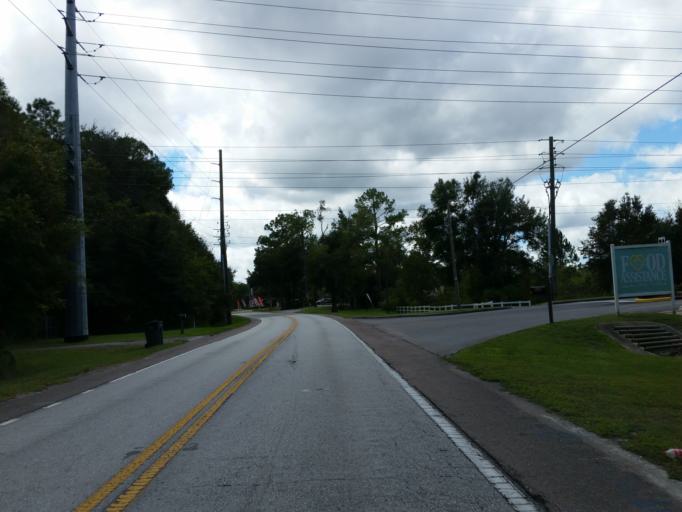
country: US
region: Florida
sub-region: Hillsborough County
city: Pebble Creek
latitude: 28.1466
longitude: -82.2804
